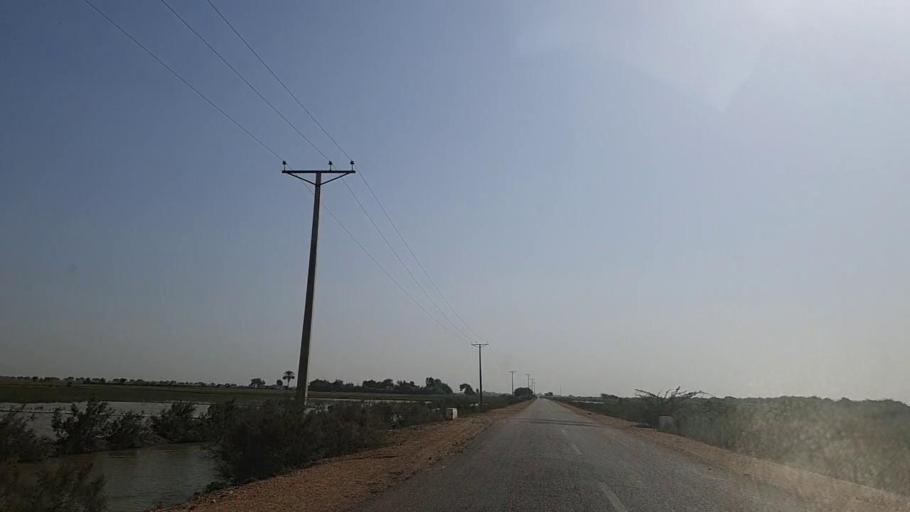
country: PK
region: Sindh
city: Mirpur Batoro
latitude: 24.5439
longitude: 68.2804
